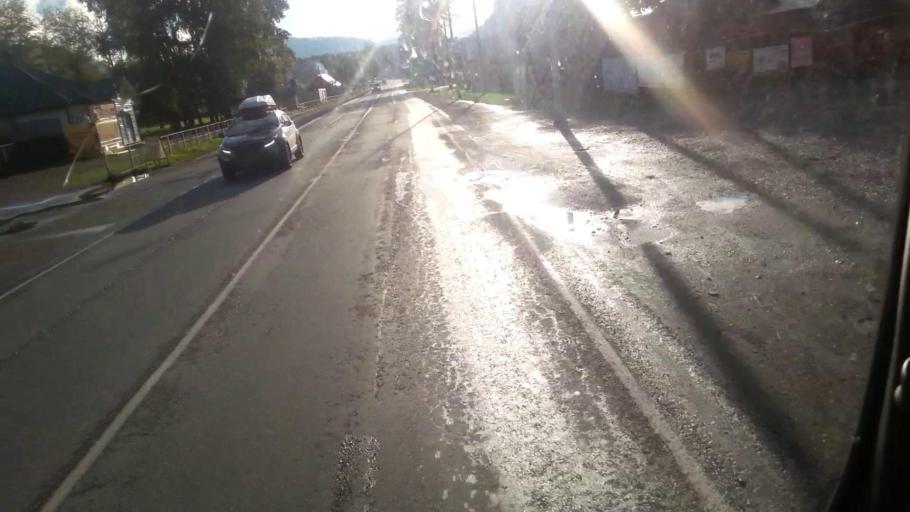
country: RU
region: Altay
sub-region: Mayminskiy Rayon
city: Manzherok
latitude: 51.8338
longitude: 85.7788
